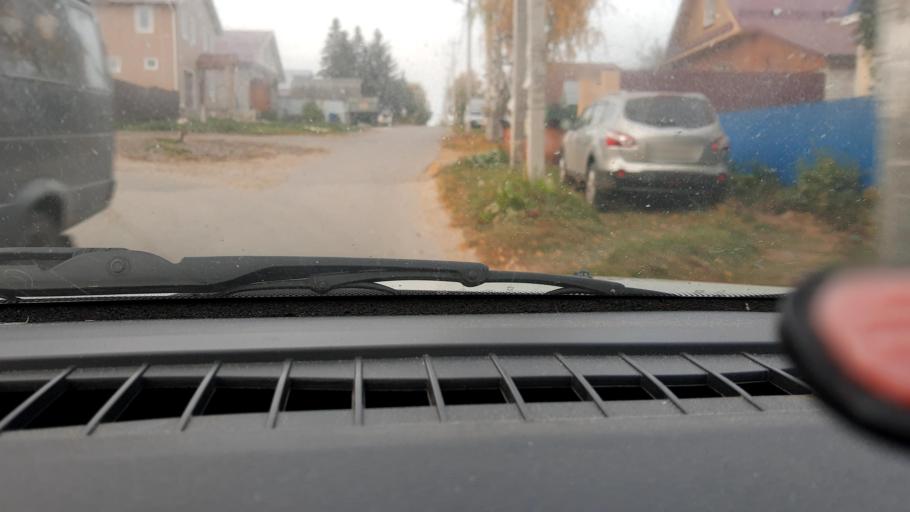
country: RU
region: Nizjnij Novgorod
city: Afonino
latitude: 56.2680
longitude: 44.0569
